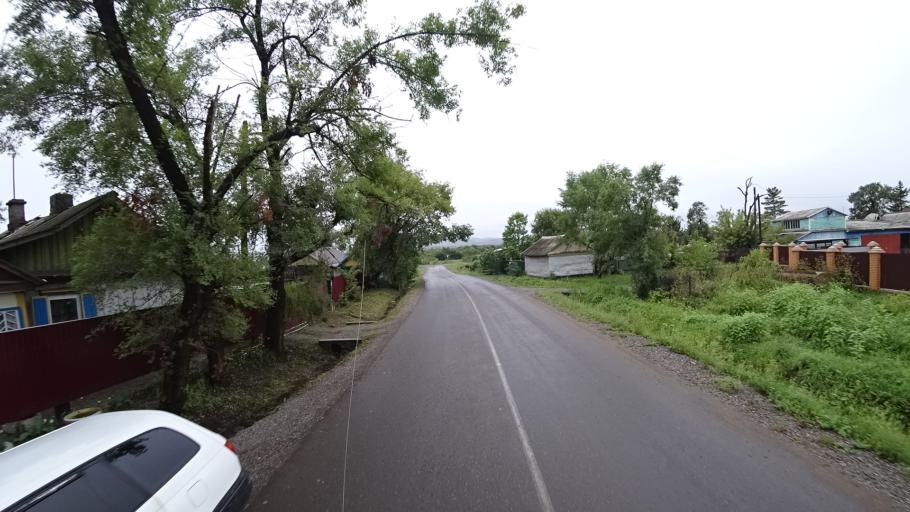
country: RU
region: Primorskiy
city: Monastyrishche
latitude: 44.2049
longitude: 132.4353
